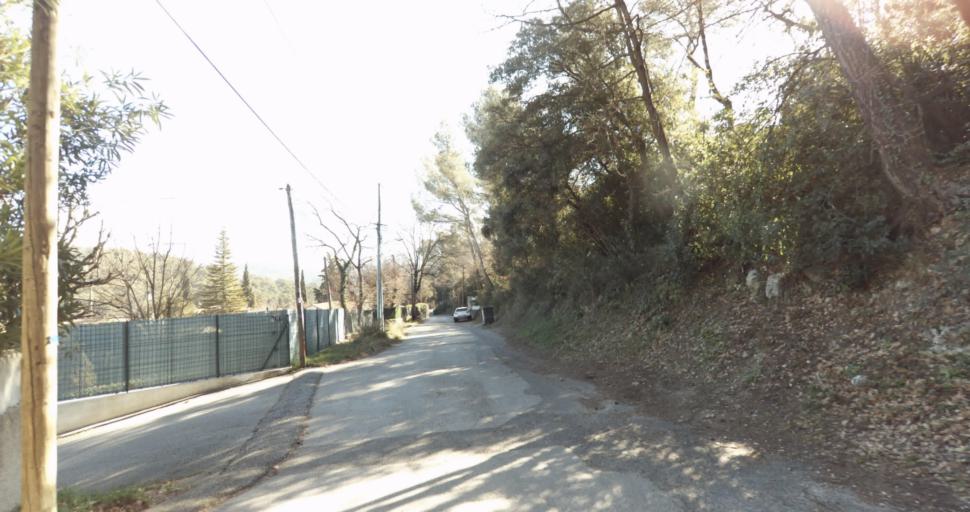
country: FR
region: Provence-Alpes-Cote d'Azur
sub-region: Departement des Bouches-du-Rhone
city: Peypin
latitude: 43.3836
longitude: 5.5835
